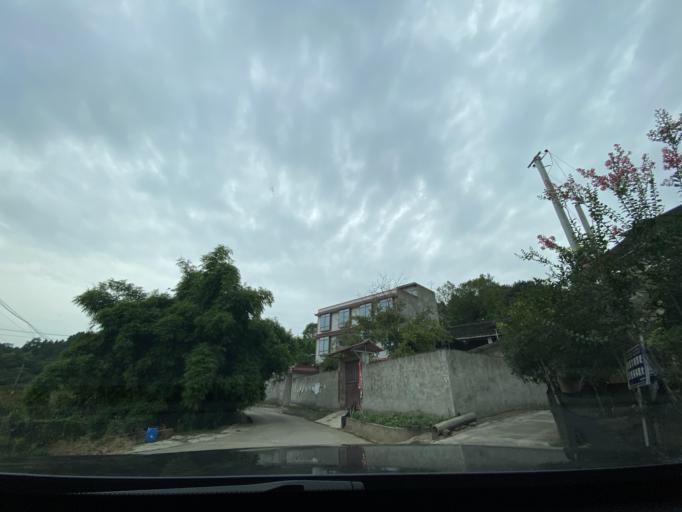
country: CN
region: Sichuan
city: Jiancheng
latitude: 30.3865
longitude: 104.4908
